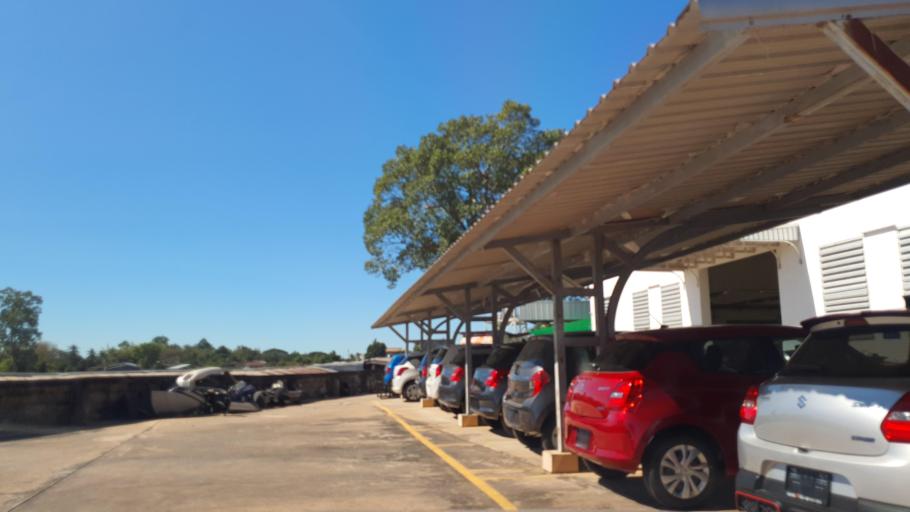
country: TH
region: Nakhon Phanom
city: Nakhon Phanom
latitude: 17.3817
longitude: 104.7533
